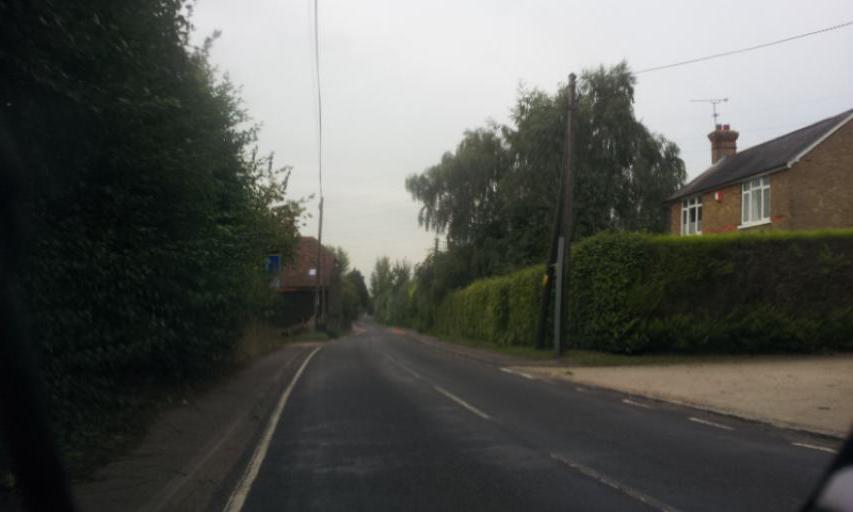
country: GB
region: England
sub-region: Kent
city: Larkfield
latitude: 51.2805
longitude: 0.4362
